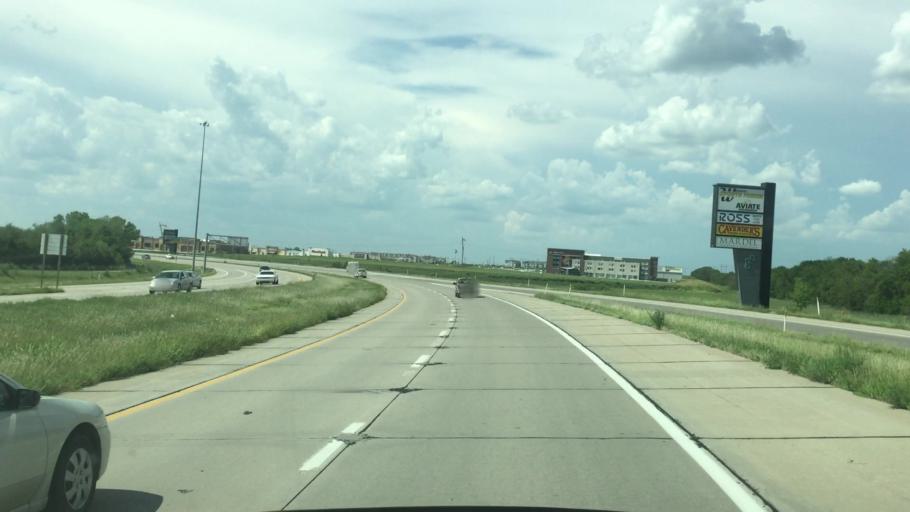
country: US
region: Kansas
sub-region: Butler County
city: Andover
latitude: 37.7254
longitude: -97.1994
